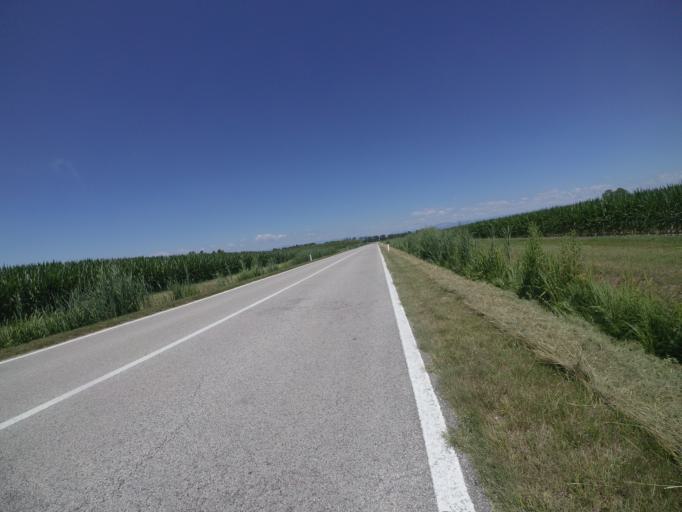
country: IT
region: Friuli Venezia Giulia
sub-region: Provincia di Udine
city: Talmassons
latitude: 45.9034
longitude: 13.0814
